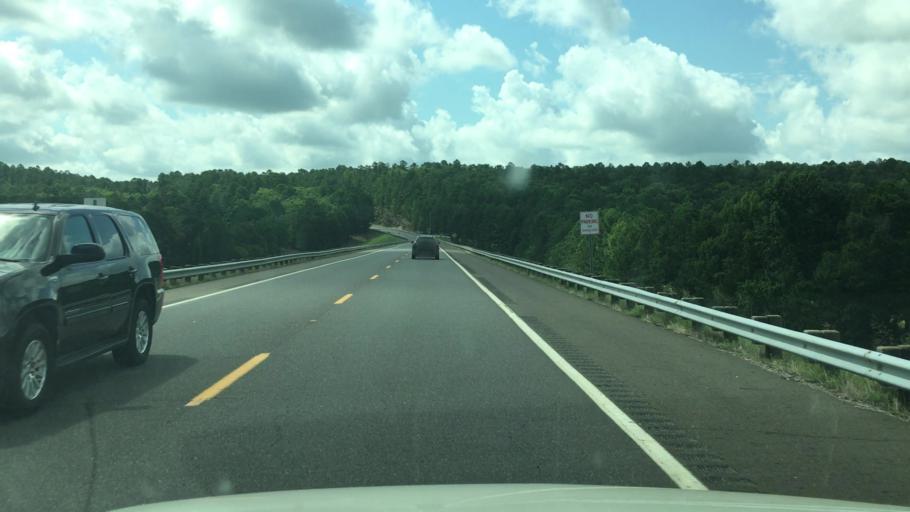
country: US
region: Arkansas
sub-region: Clark County
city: Arkadelphia
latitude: 34.2365
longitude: -93.1020
